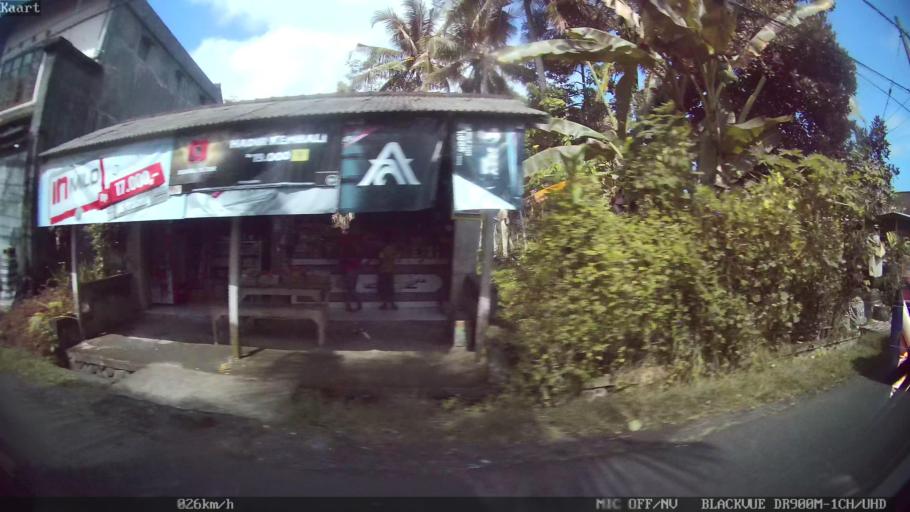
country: ID
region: Bali
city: Banjar Apuan Kaja
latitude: -8.5174
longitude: 115.3297
